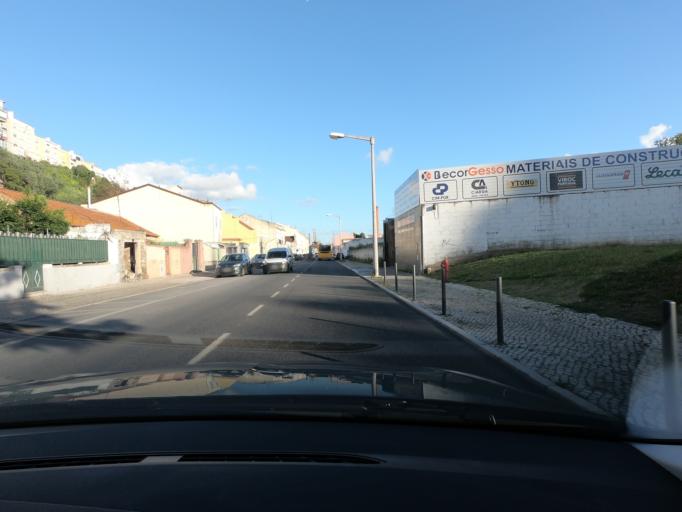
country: PT
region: Lisbon
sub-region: Lisbon
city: Lisbon
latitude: 38.7307
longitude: -9.1165
